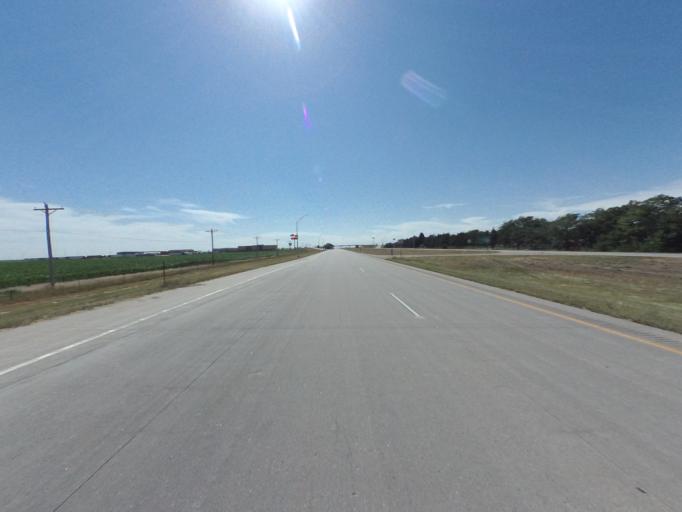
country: US
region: Colorado
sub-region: Kit Carson County
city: Burlington
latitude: 39.2940
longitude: -102.2728
